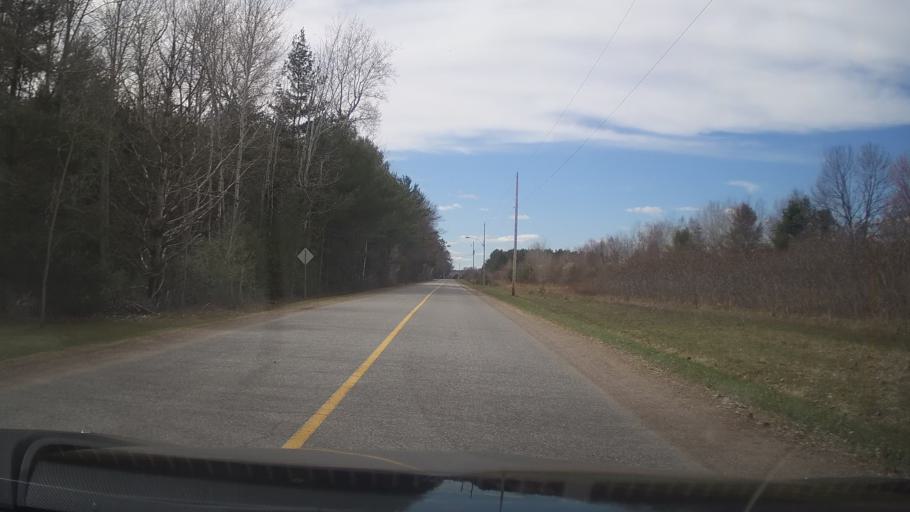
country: CA
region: Ontario
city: Arnprior
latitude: 45.5187
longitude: -76.4082
